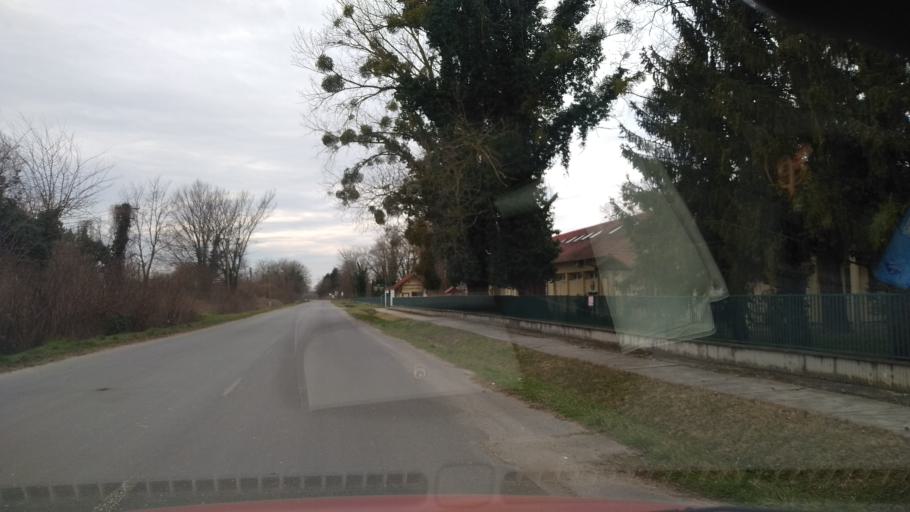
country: HU
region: Somogy
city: Barcs
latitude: 45.9536
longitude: 17.4374
